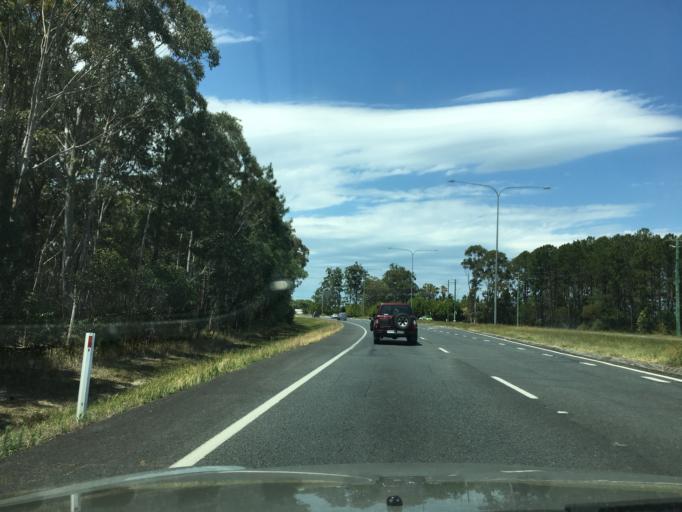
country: AU
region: Queensland
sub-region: Moreton Bay
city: Caboolture
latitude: -27.0757
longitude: 153.0505
